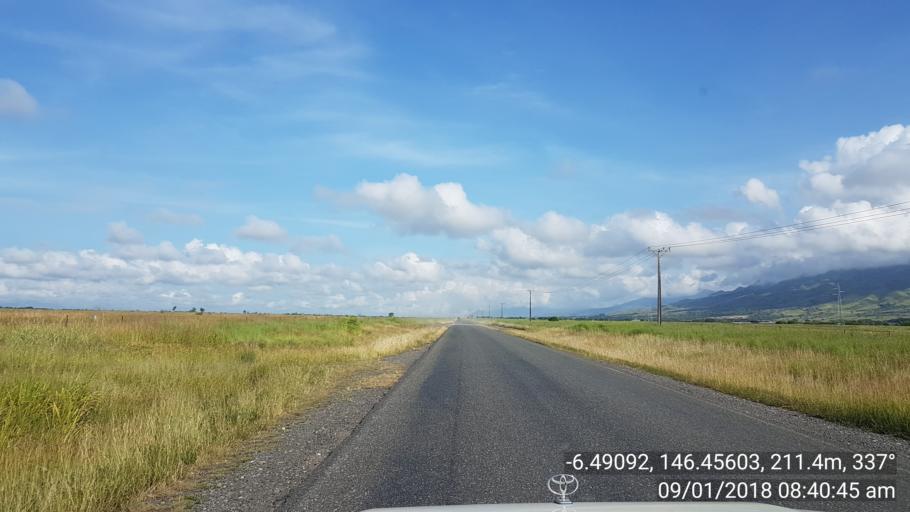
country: PG
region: Morobe
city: Lae
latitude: -6.4909
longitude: 146.4559
